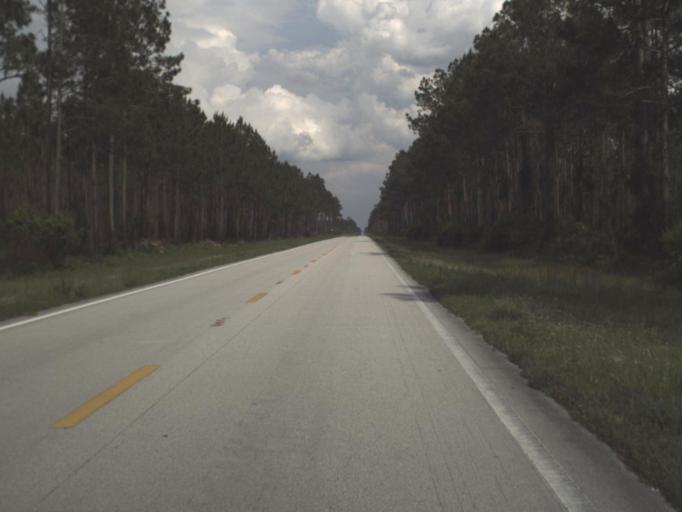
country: US
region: Florida
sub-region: Baker County
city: Macclenny
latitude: 30.5490
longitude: -82.3562
